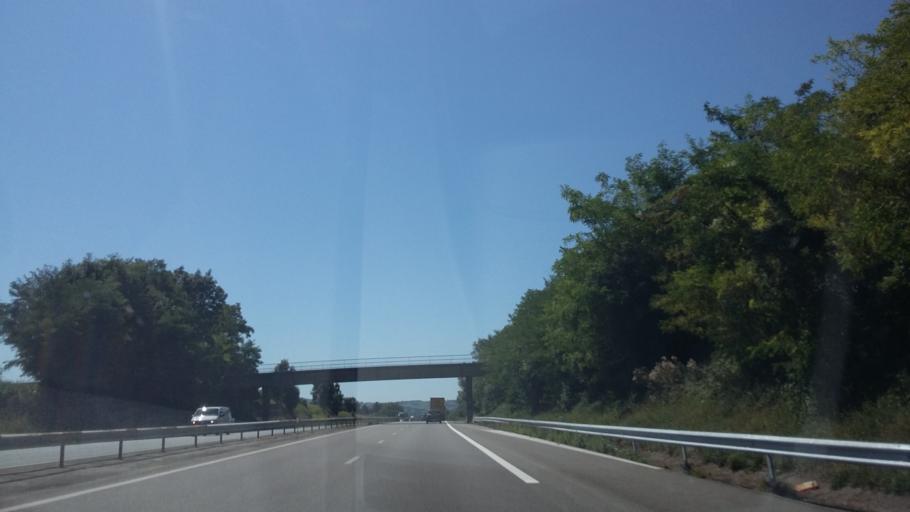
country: FR
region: Rhone-Alpes
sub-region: Departement de l'Isere
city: Saint-Victor-de-Cessieu
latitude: 45.5152
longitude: 5.4072
